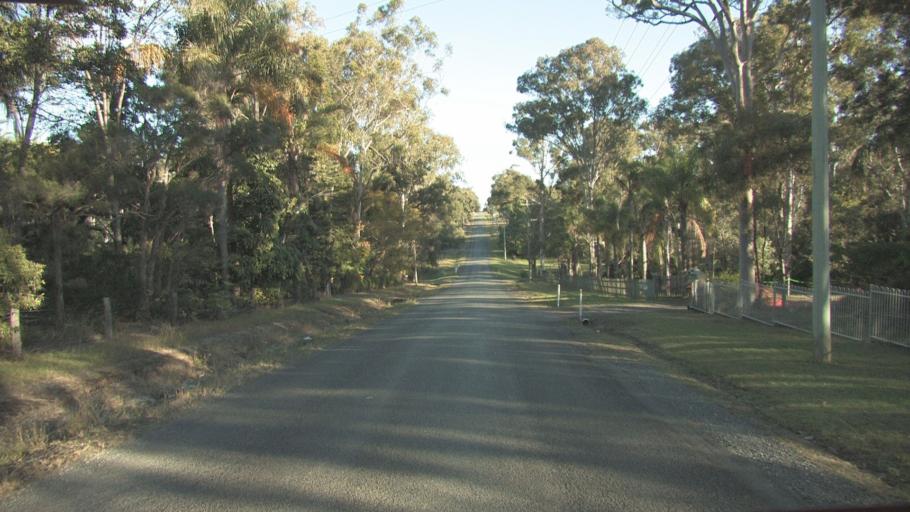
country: AU
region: Queensland
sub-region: Logan
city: Waterford West
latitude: -27.7212
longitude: 153.1540
